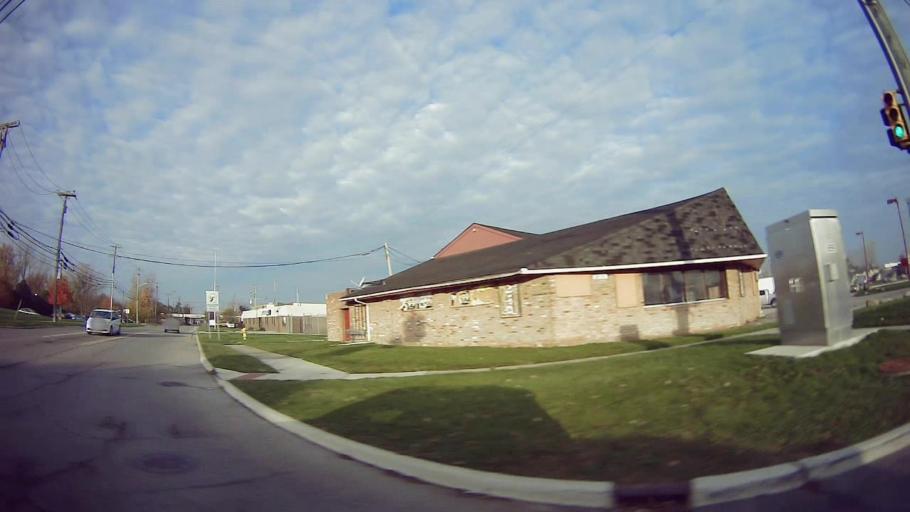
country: US
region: Michigan
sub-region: Macomb County
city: Mount Clemens
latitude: 42.5479
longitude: -82.8757
